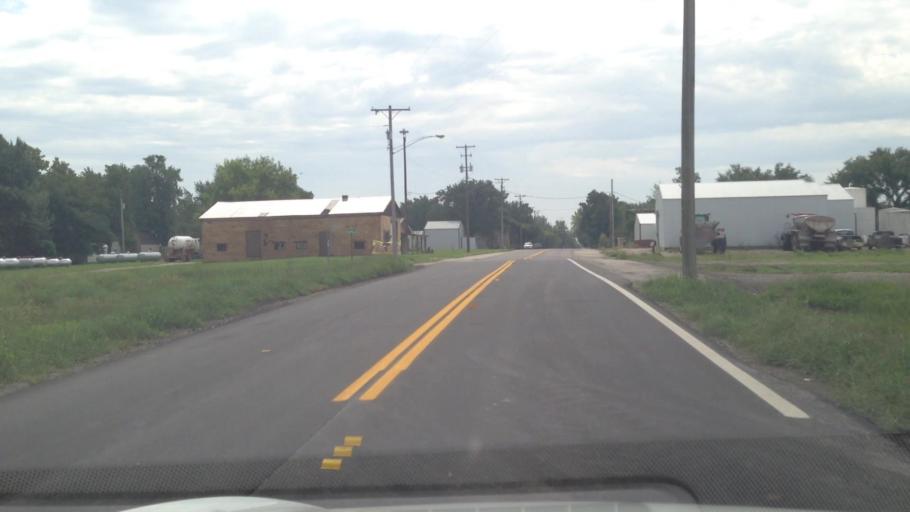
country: US
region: Kansas
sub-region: Crawford County
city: Girard
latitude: 37.6643
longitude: -94.9696
